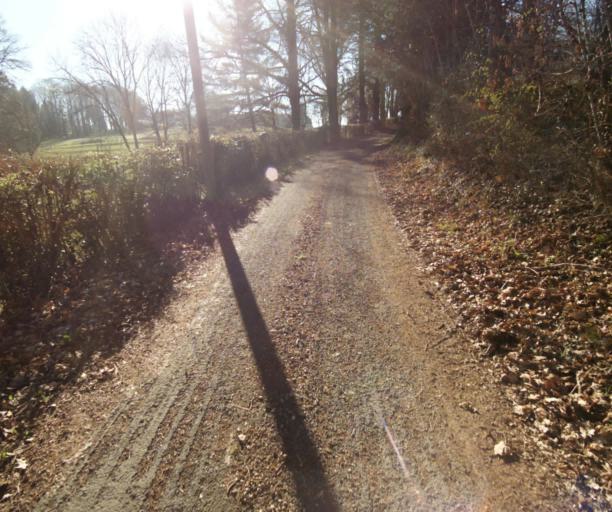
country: FR
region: Limousin
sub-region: Departement de la Correze
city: Chamboulive
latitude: 45.4176
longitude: 1.6886
